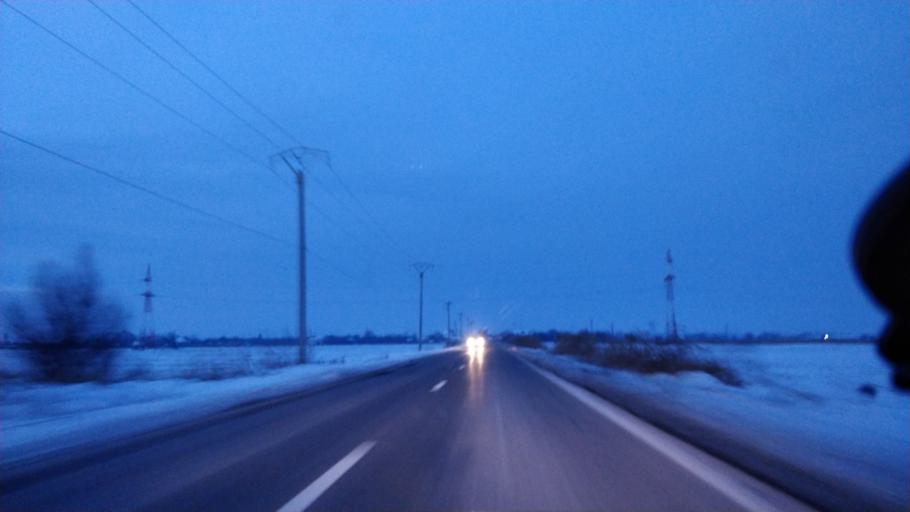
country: RO
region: Vrancea
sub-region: Comuna Nanesti
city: Nanesti
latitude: 45.5809
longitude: 27.4972
